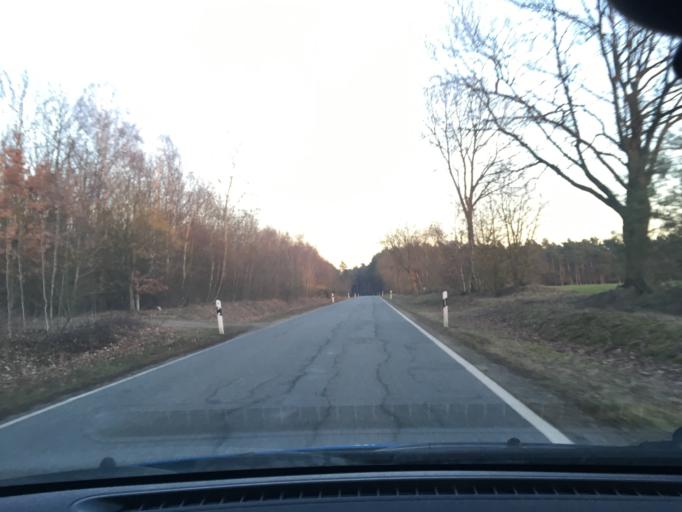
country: DE
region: Schleswig-Holstein
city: Brothen
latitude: 53.4849
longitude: 10.6813
